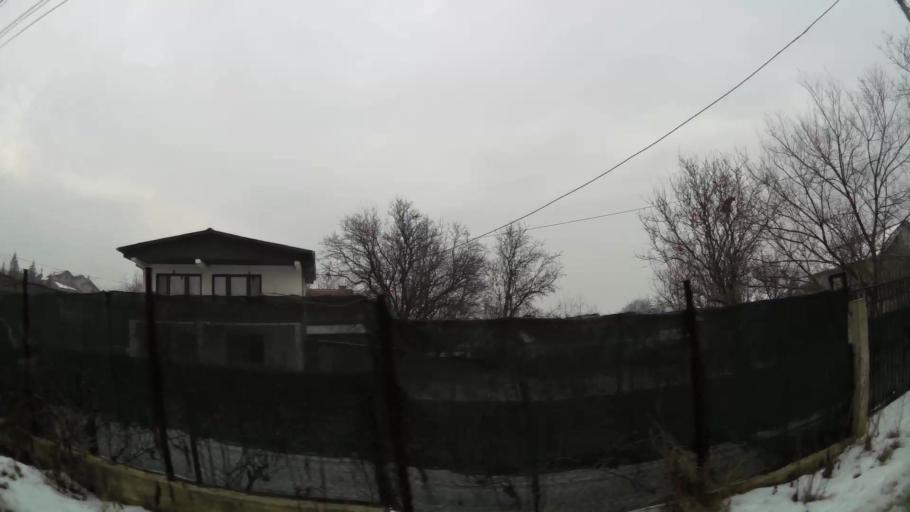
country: MK
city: Kondovo
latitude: 42.0488
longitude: 21.3424
